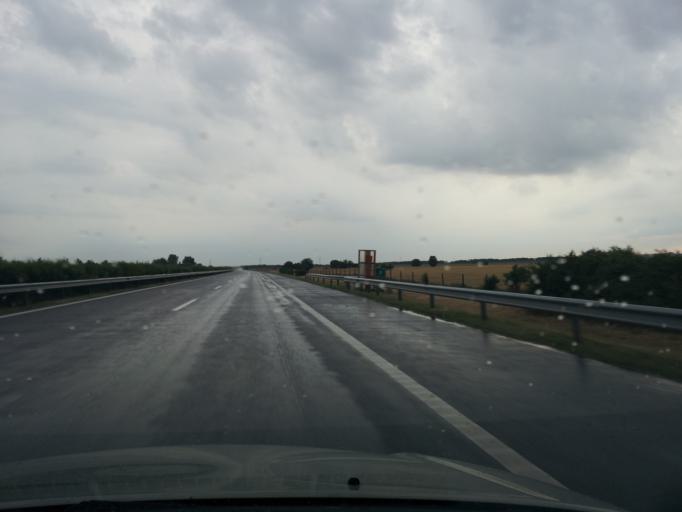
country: HU
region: Borsod-Abauj-Zemplen
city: Emod
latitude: 47.9376
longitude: 20.8645
